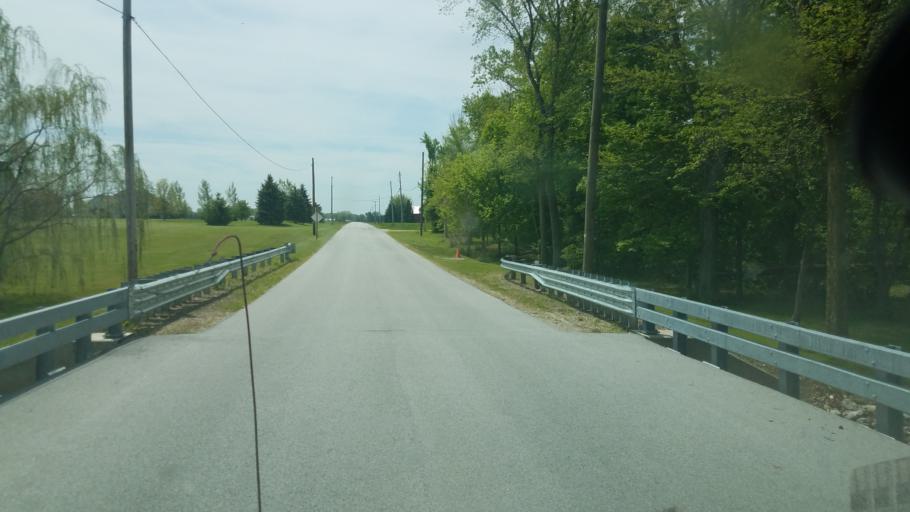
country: US
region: Ohio
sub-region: Ottawa County
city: Oak Harbor
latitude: 41.4969
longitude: -83.1643
